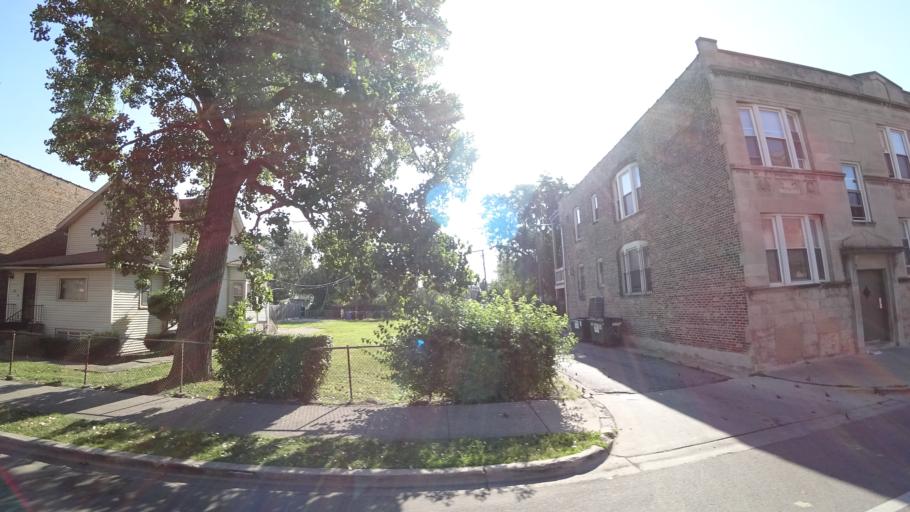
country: US
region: Illinois
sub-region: Cook County
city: Cicero
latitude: 41.8521
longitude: -87.7150
